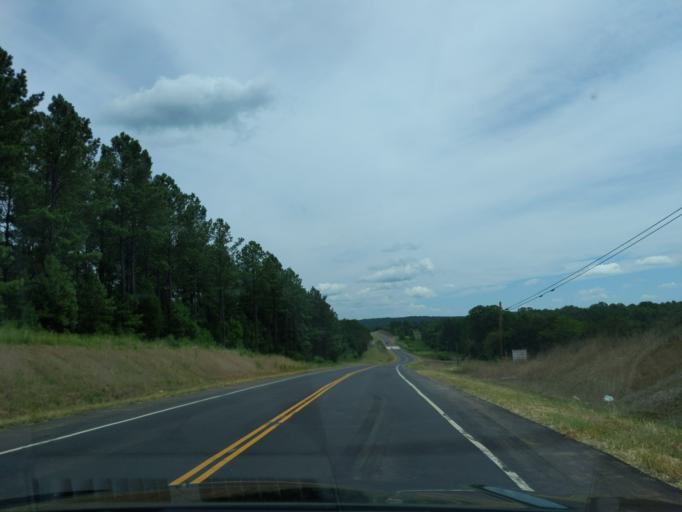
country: US
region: North Carolina
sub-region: Cabarrus County
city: Mount Pleasant
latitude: 35.4239
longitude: -80.4158
